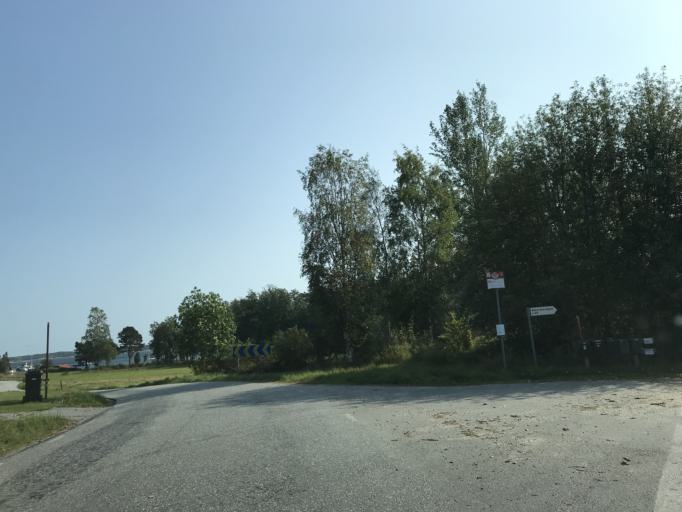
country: SE
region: Stockholm
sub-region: Norrtalje Kommun
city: Bjorko
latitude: 59.8718
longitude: 19.0681
